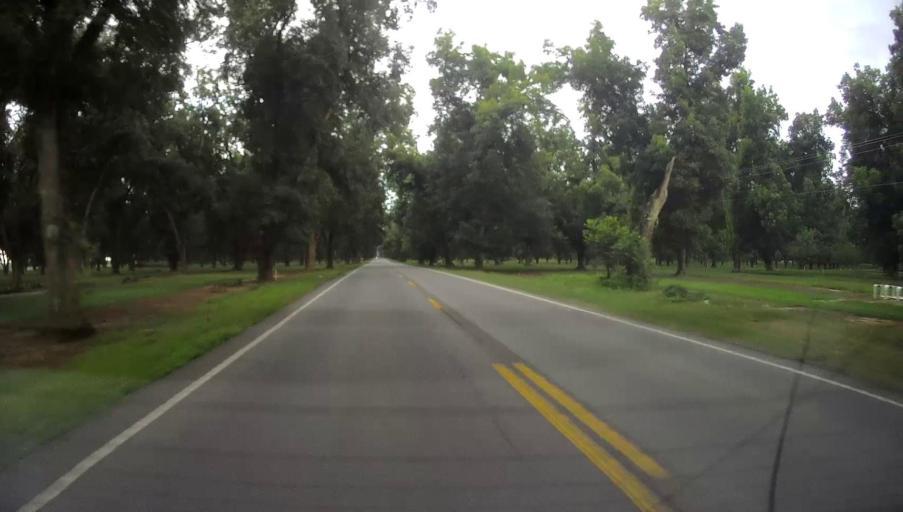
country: US
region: Georgia
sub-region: Houston County
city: Perry
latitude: 32.4427
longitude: -83.6597
